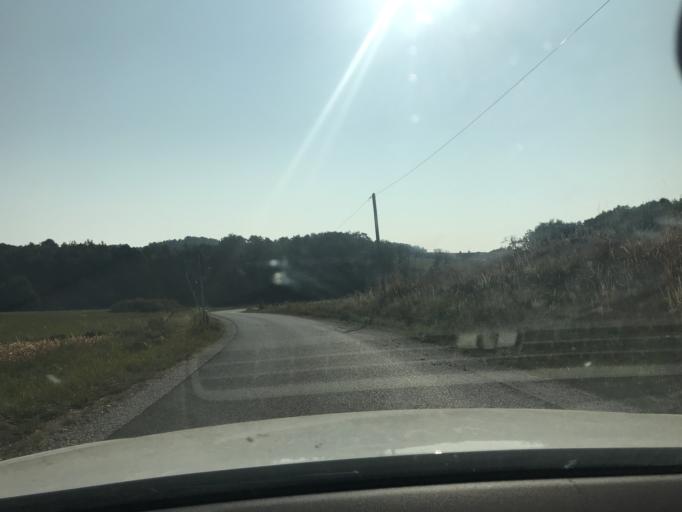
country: DE
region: Bavaria
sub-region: Upper Palatinate
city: Auerbach
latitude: 49.7367
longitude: 11.6005
